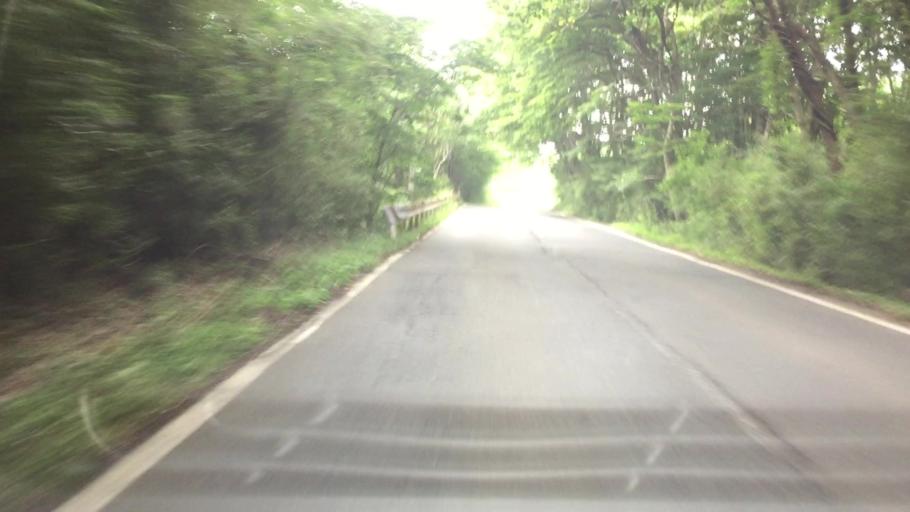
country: JP
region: Tochigi
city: Kuroiso
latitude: 37.0870
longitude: 140.0589
